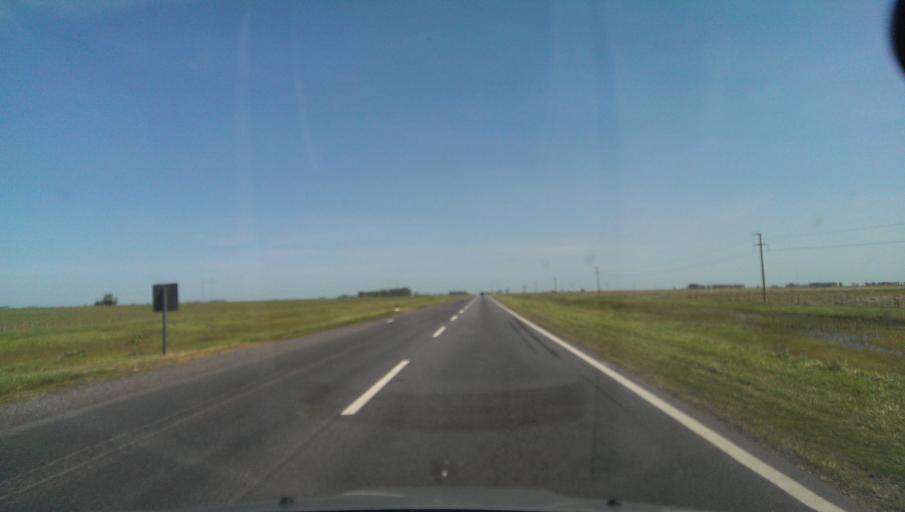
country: AR
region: Buenos Aires
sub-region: Partido de Azul
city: Azul
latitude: -36.5775
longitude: -59.6438
